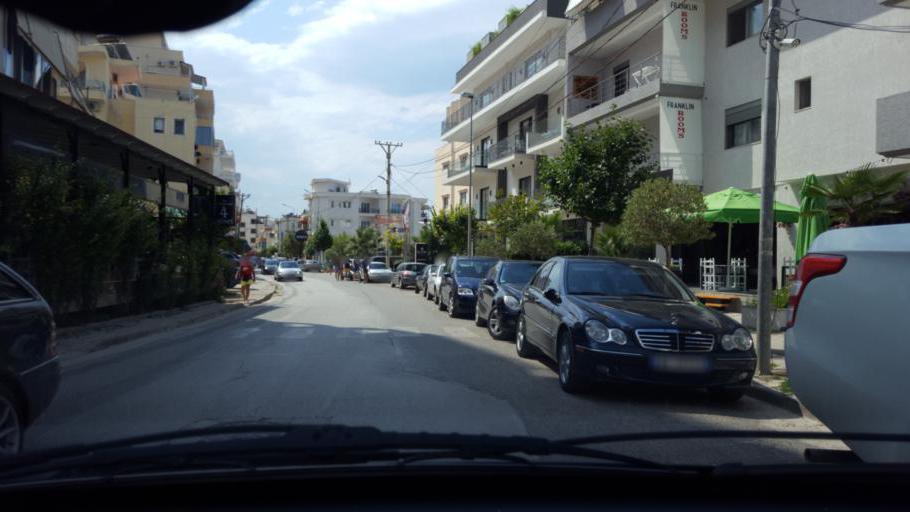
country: AL
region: Vlore
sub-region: Rrethi i Sarandes
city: Sarande
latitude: 39.8554
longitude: 20.0216
